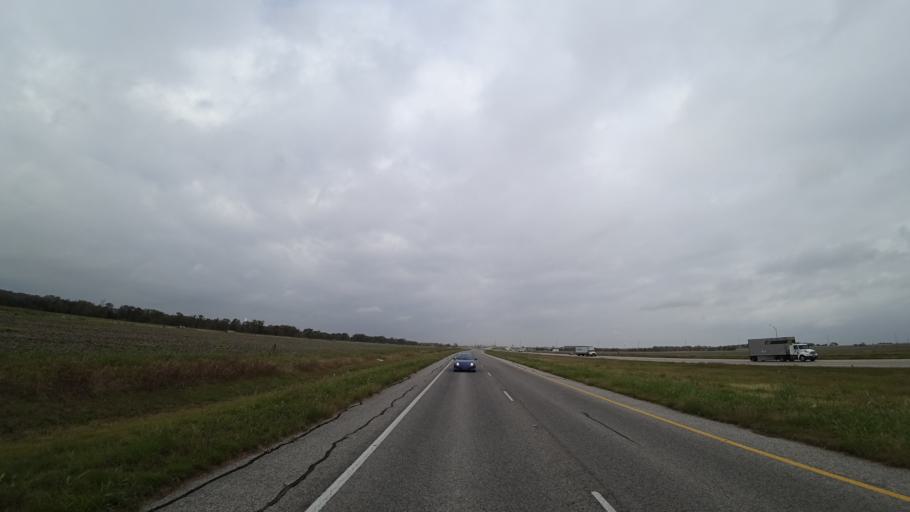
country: US
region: Texas
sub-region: Travis County
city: Pflugerville
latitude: 30.4377
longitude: -97.5925
